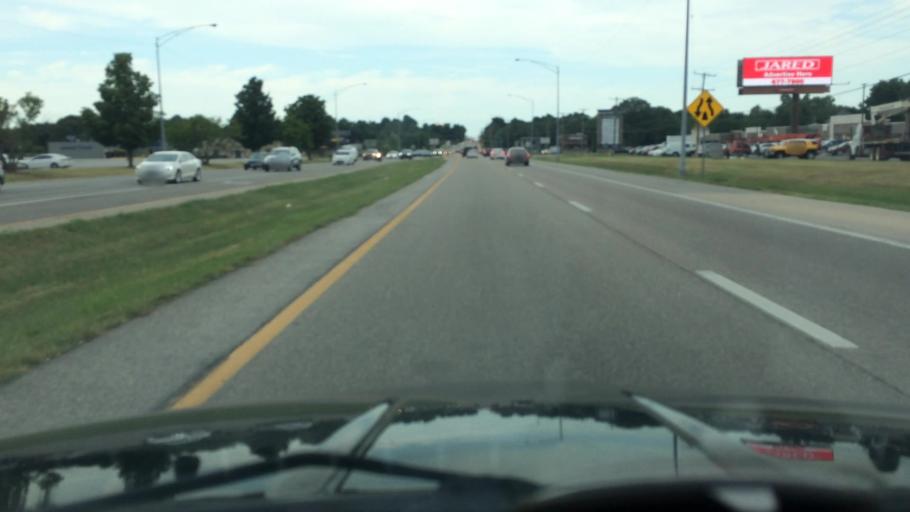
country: US
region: Missouri
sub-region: Greene County
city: Springfield
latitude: 37.1635
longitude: -93.2626
